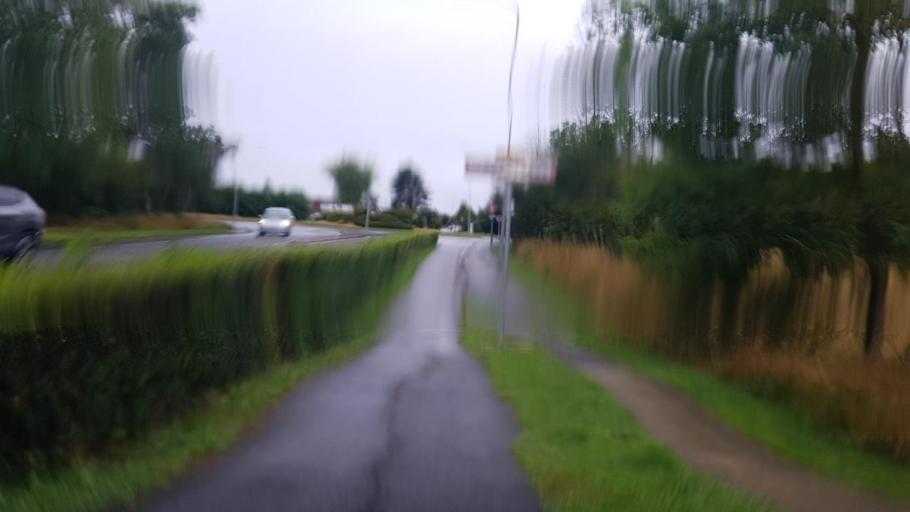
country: FR
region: Champagne-Ardenne
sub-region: Departement de la Marne
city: Saint-Memmie
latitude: 48.9335
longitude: 4.3898
